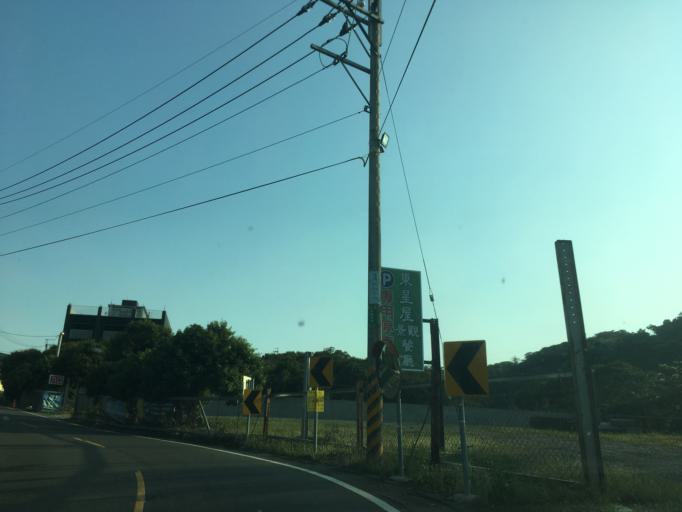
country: TW
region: Taiwan
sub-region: Nantou
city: Nantou
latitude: 23.9436
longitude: 120.6515
